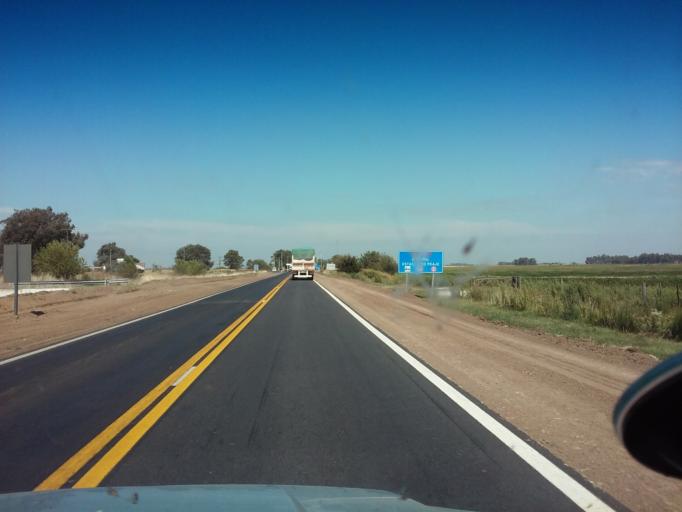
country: AR
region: Buenos Aires
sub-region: Partido de Nueve de Julio
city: Nueve de Julio
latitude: -35.3567
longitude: -60.6986
